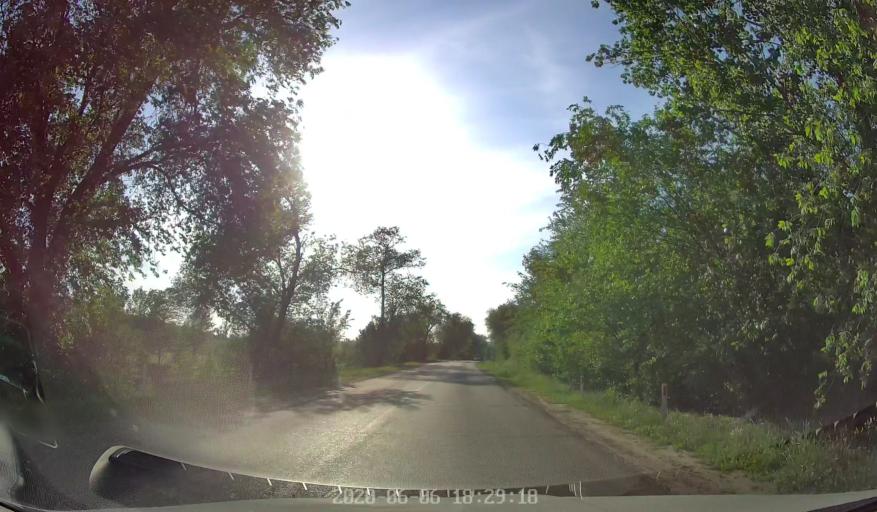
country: MD
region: Chisinau
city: Ciorescu
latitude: 47.1321
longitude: 28.9715
